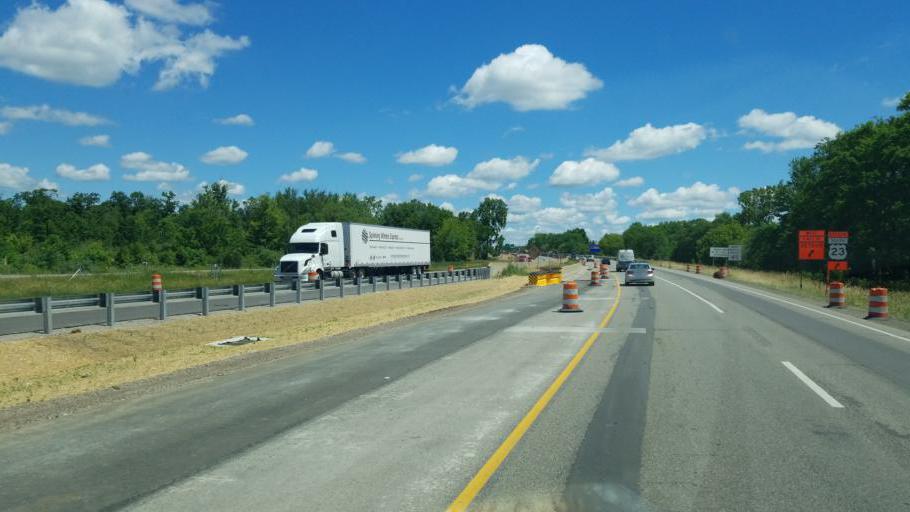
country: US
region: Michigan
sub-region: Livingston County
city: Whitmore Lake
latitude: 42.4359
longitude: -83.7588
